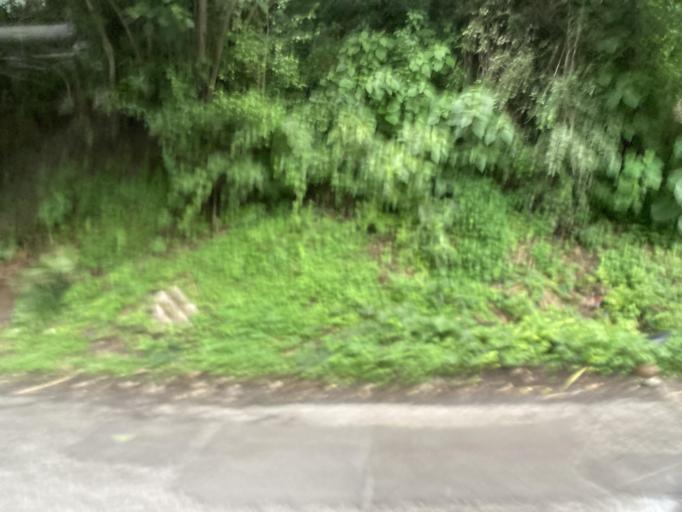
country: GT
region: Guatemala
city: Villa Canales
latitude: 14.4266
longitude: -90.5344
